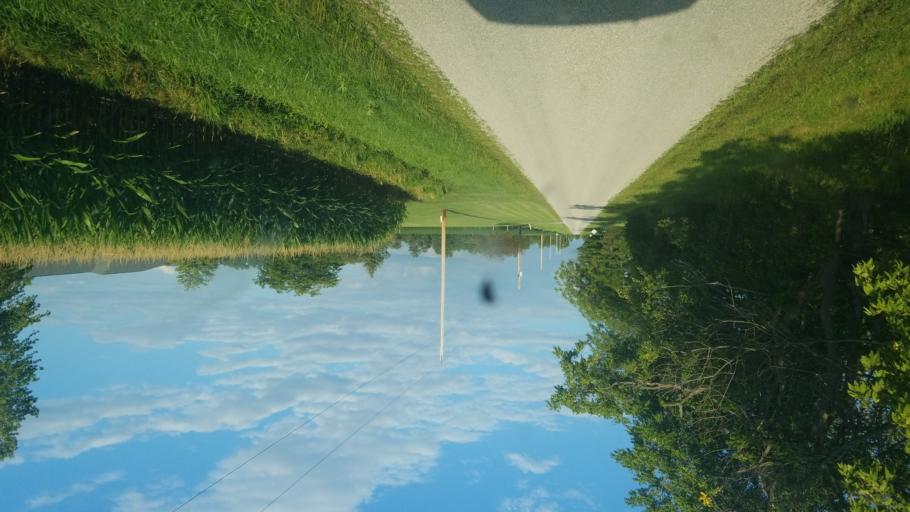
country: US
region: Ohio
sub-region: Sandusky County
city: Mount Carmel
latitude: 41.1101
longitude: -82.9246
